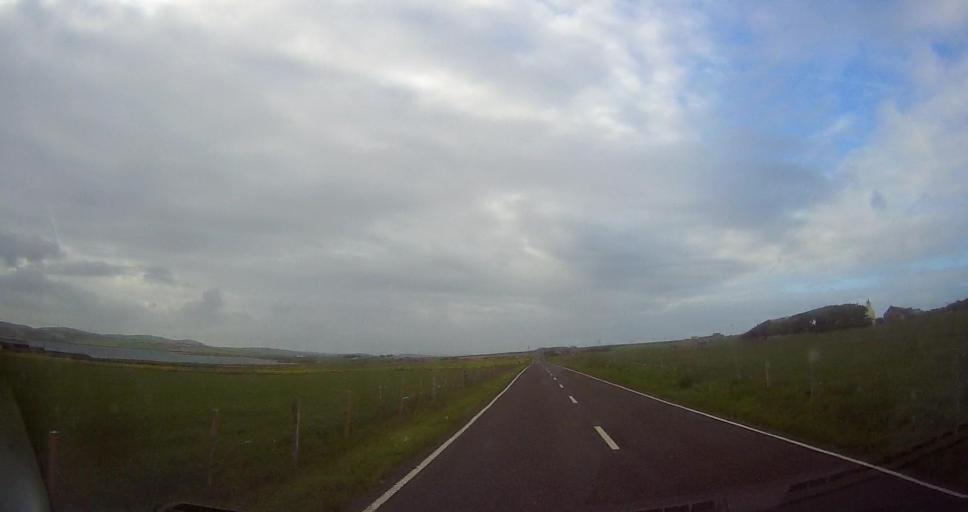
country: GB
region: Scotland
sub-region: Orkney Islands
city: Stromness
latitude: 58.9621
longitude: -3.2232
